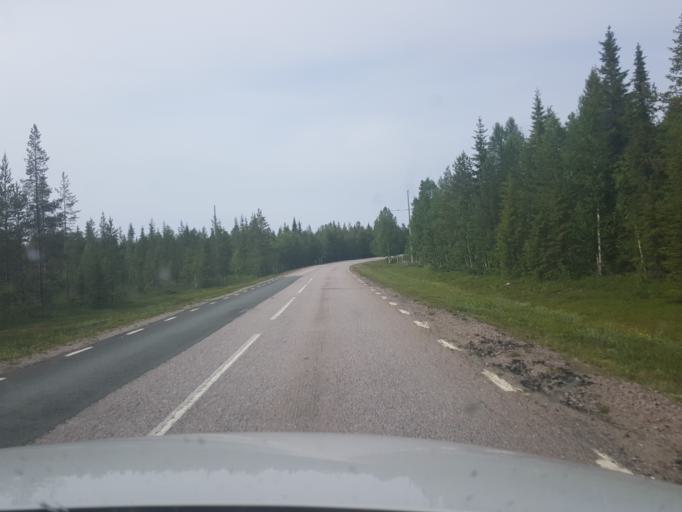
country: SE
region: Norrbotten
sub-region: Arjeplogs Kommun
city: Arjeplog
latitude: 65.8022
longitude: 18.0045
